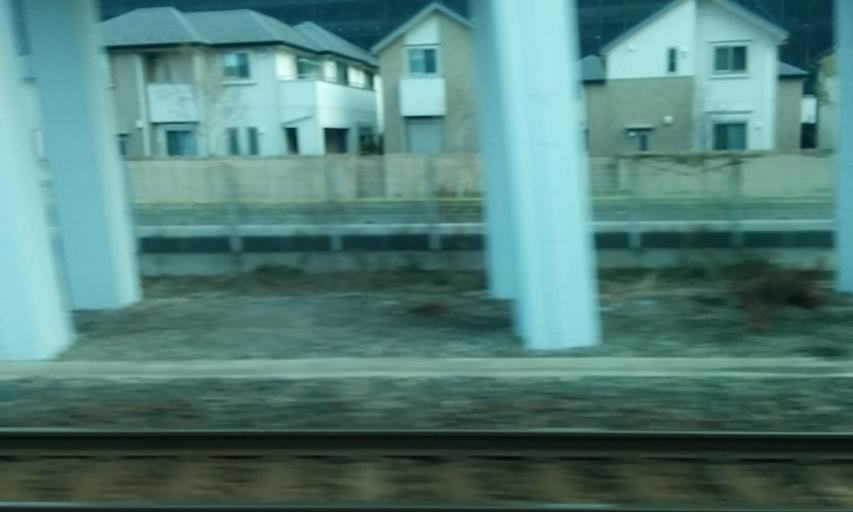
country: JP
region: Saitama
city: Kawaguchi
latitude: 35.8085
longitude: 139.7115
